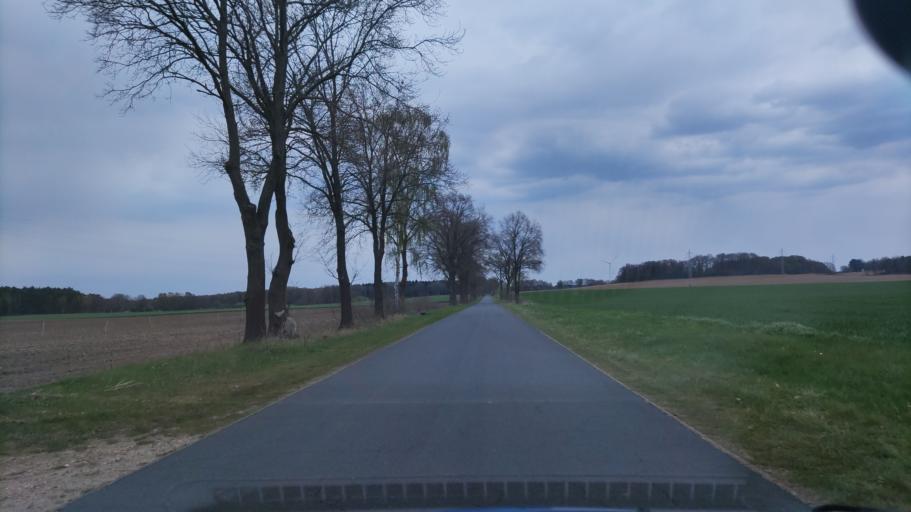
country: DE
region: Lower Saxony
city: Oldendorf
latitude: 53.1578
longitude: 10.2236
